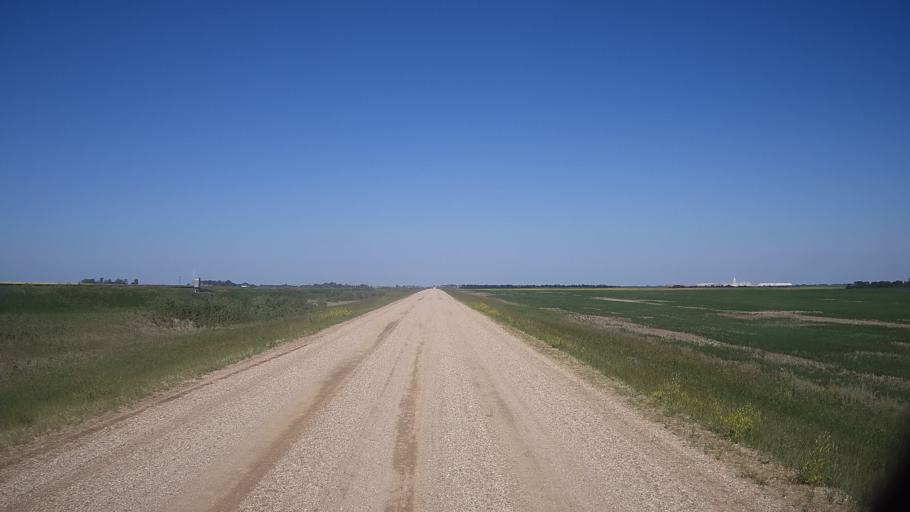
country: CA
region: Saskatchewan
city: Watrous
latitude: 51.8692
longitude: -105.9884
